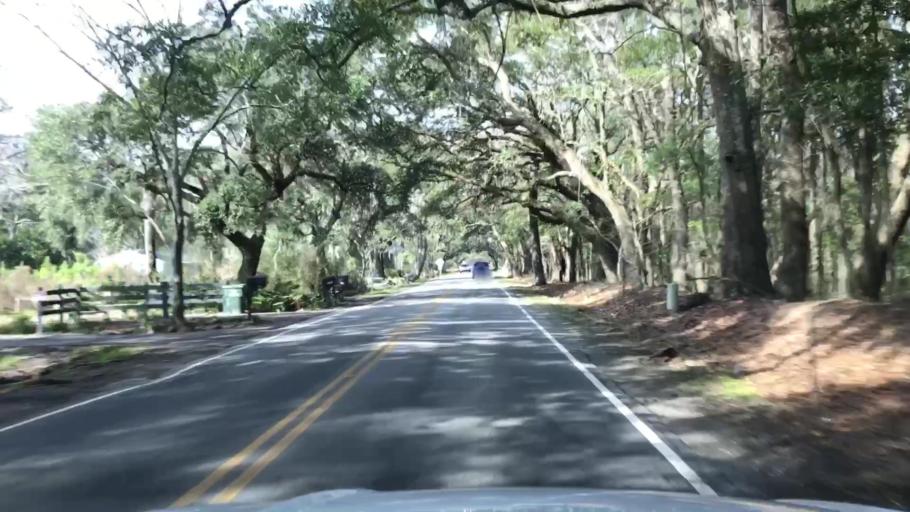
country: US
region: South Carolina
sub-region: Charleston County
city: Shell Point
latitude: 32.7530
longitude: -80.0460
